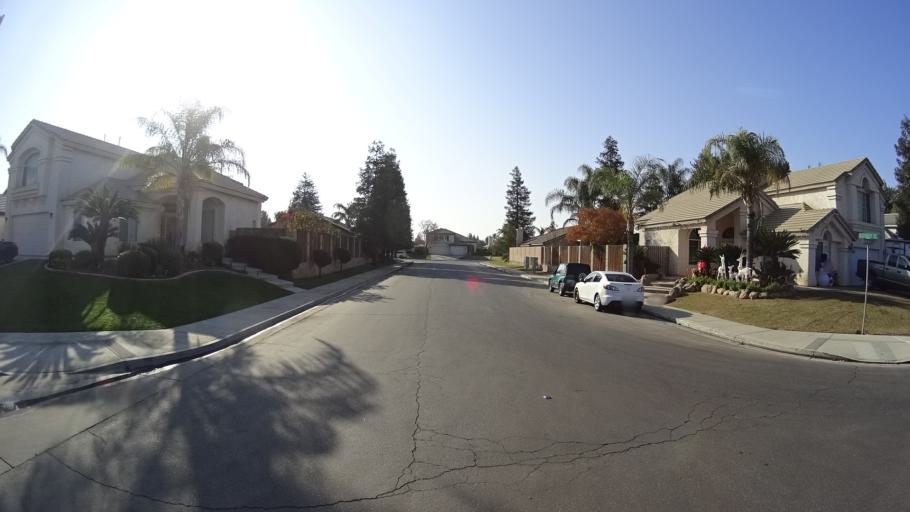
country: US
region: California
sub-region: Kern County
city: Greenacres
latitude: 35.3674
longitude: -119.1172
